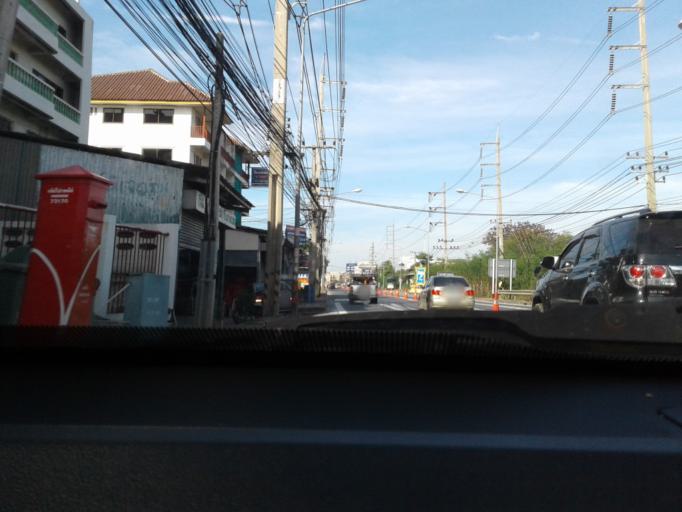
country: TH
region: Nakhon Pathom
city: Salaya
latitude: 13.8058
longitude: 100.3218
